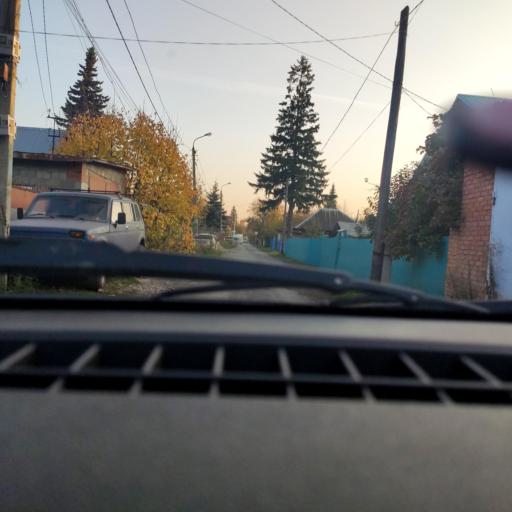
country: RU
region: Bashkortostan
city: Ufa
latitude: 54.7998
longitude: 56.1465
